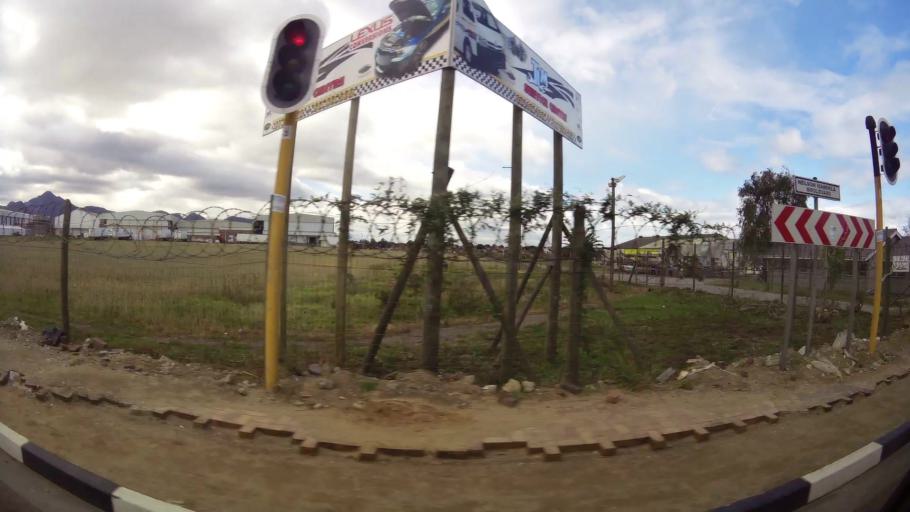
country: ZA
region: Western Cape
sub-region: Eden District Municipality
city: George
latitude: -33.9787
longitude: 22.4718
